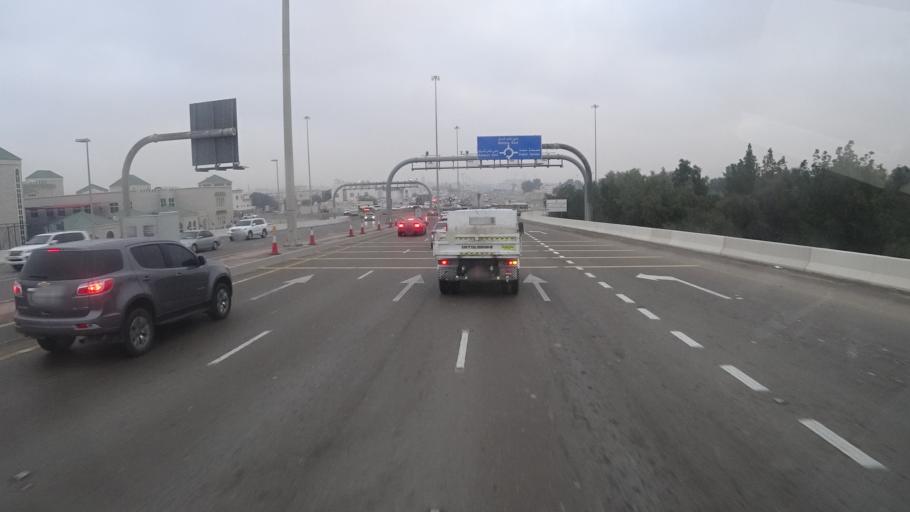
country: AE
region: Abu Dhabi
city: Abu Dhabi
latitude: 24.2824
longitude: 54.6492
